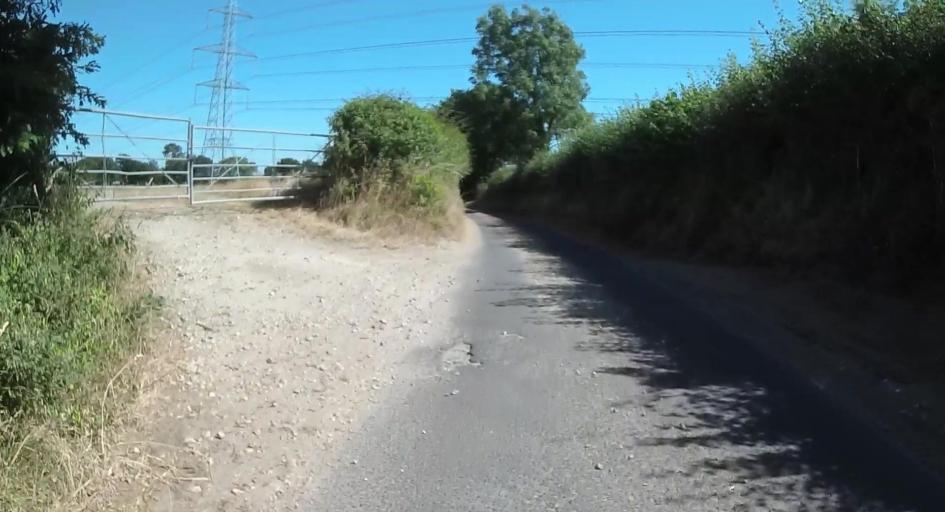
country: GB
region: England
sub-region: Dorset
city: Bovington Camp
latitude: 50.7263
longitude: -2.2003
